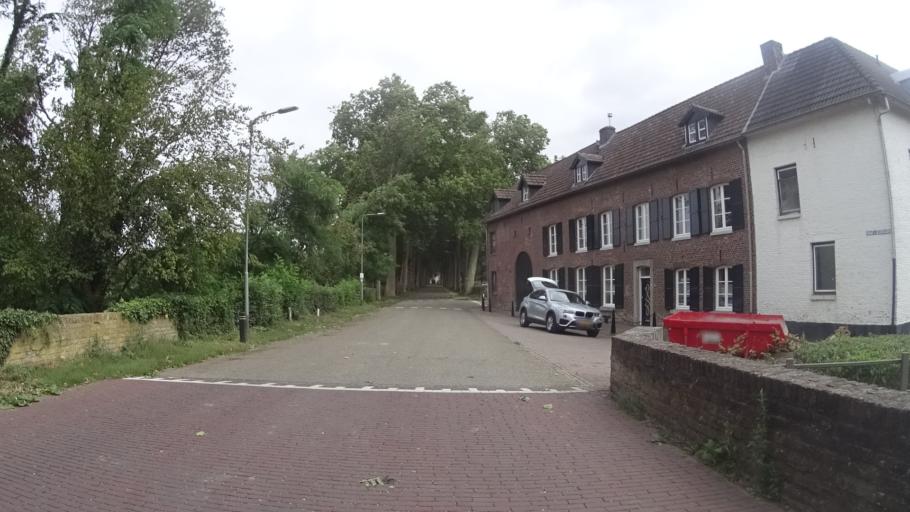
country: NL
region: Limburg
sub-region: Eijsden-Margraten
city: Eijsden
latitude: 50.7708
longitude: 5.6997
